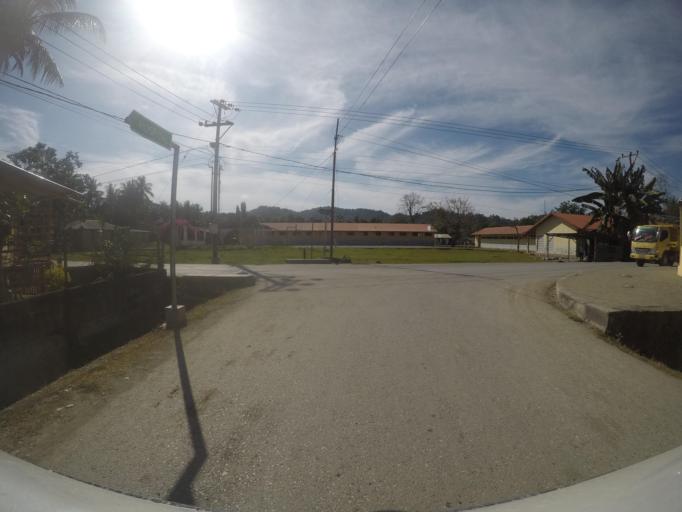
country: TL
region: Viqueque
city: Viqueque
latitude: -8.8553
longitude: 126.3636
